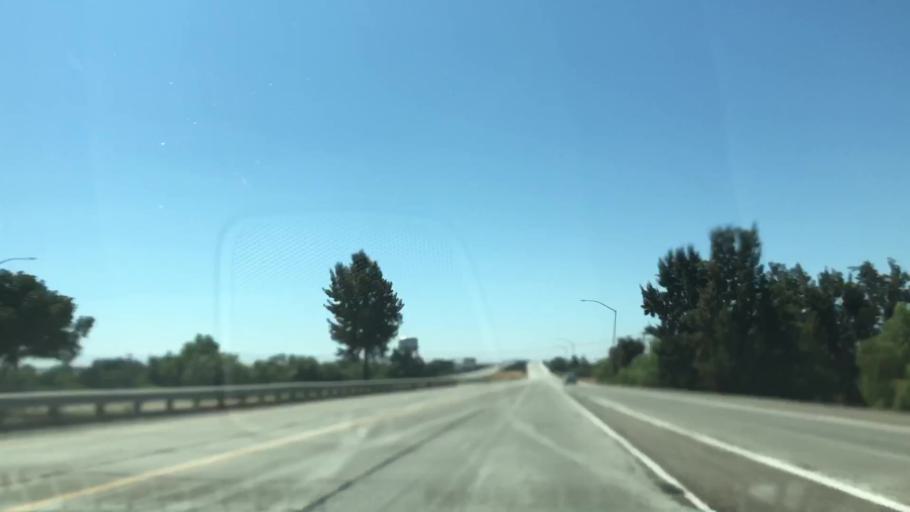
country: US
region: California
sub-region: San Joaquin County
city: Stockton
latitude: 37.9460
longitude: -121.3079
